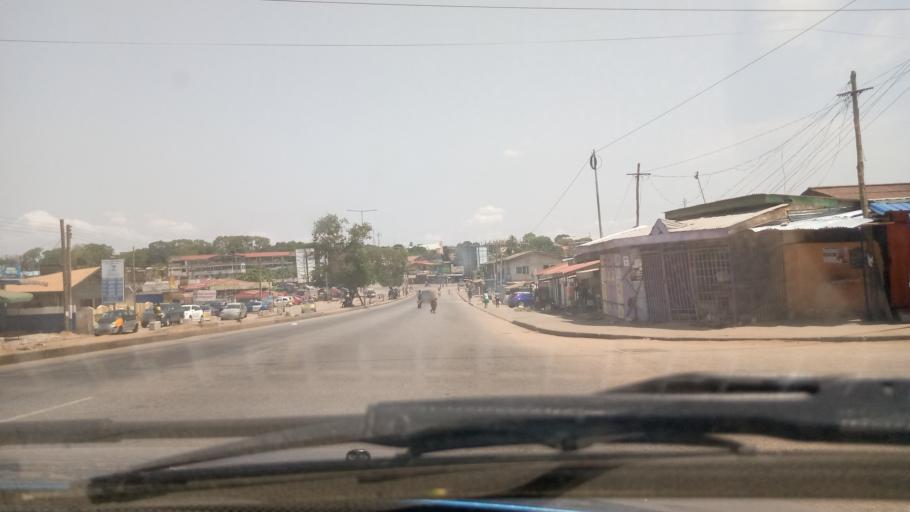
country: GH
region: Greater Accra
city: Accra
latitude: 5.5672
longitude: -0.2430
